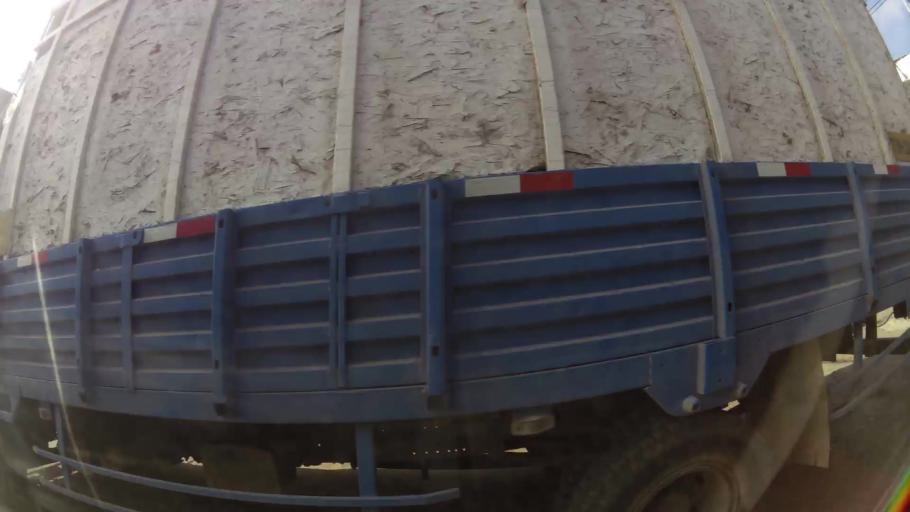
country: PE
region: La Libertad
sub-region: Provincia de Trujillo
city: El Porvenir
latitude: -8.1016
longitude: -79.0076
